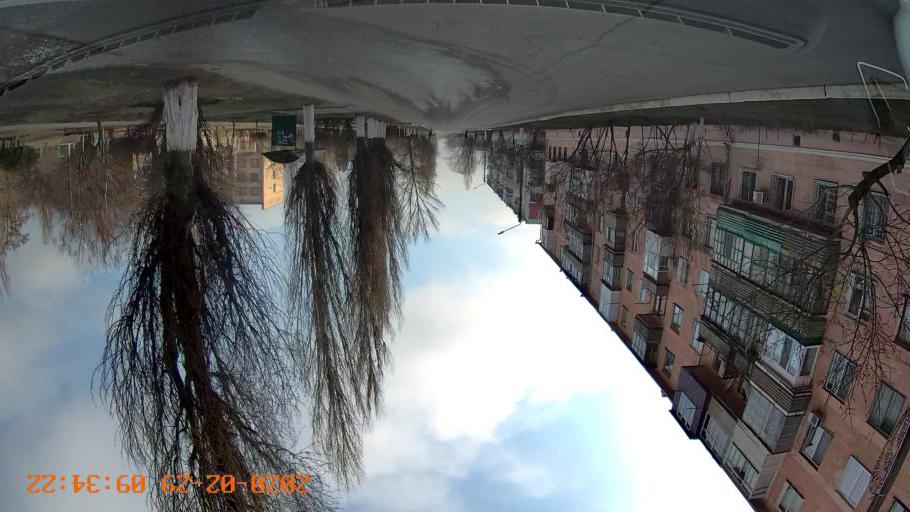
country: MD
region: Telenesti
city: Dnestrovsc
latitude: 46.6244
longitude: 29.9038
